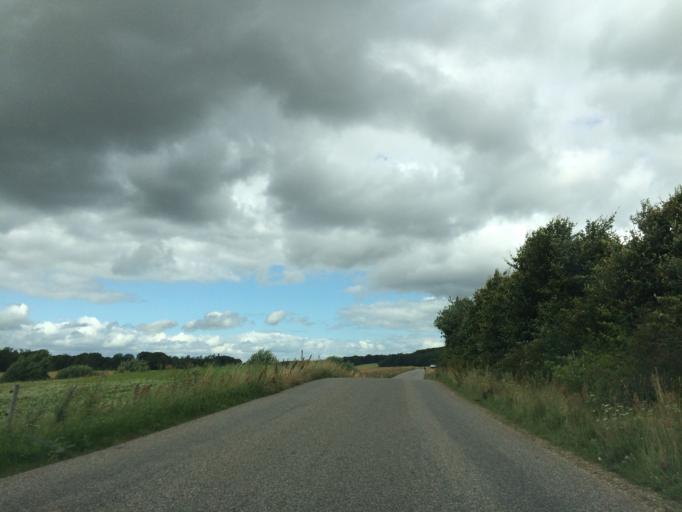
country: DK
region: Central Jutland
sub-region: Silkeborg Kommune
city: Svejbaek
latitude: 56.2417
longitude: 9.6777
